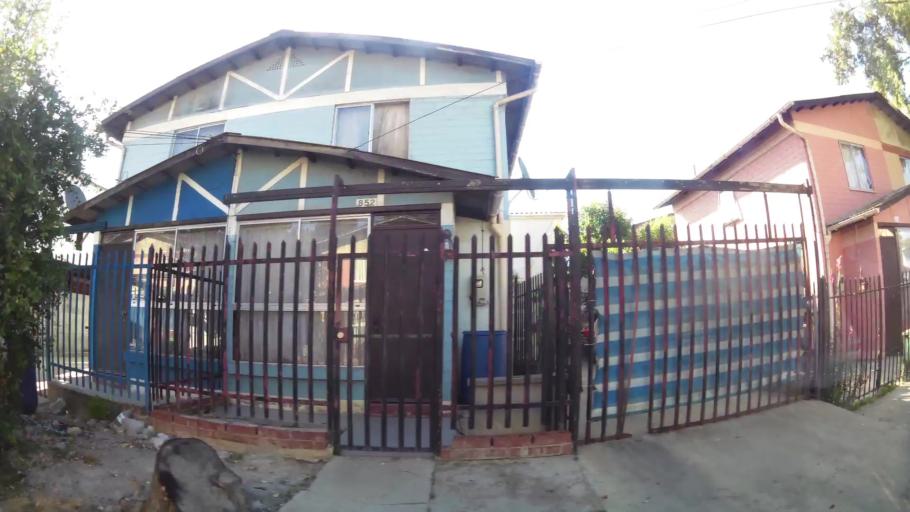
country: CL
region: Valparaiso
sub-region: Provincia de Valparaiso
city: Valparaiso
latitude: -33.1155
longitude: -71.5777
